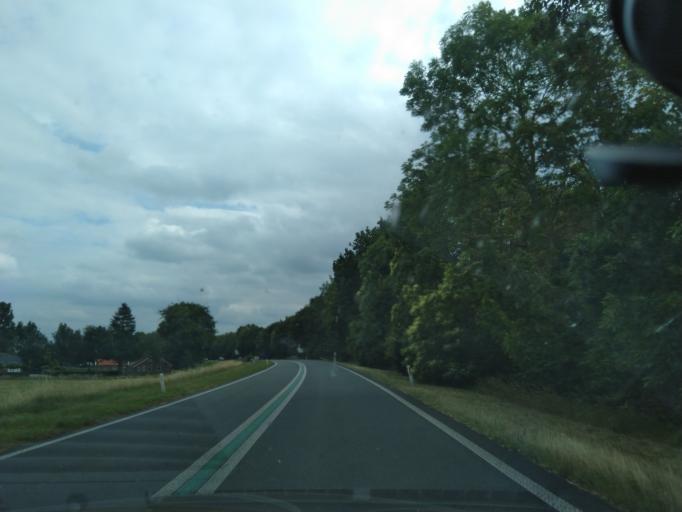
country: NL
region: Groningen
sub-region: Gemeente  Oldambt
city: Winschoten
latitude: 53.1069
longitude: 7.0675
